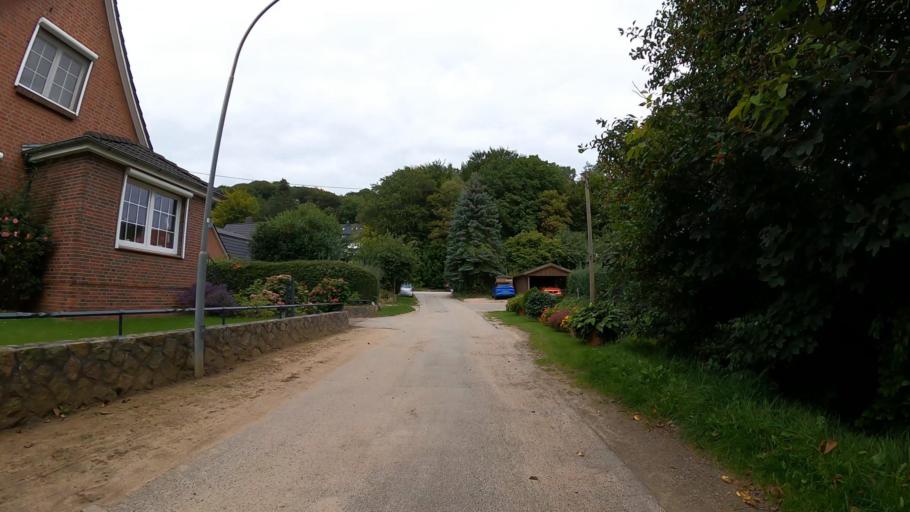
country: DE
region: Schleswig-Holstein
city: Bornsen
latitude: 53.4661
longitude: 10.2915
